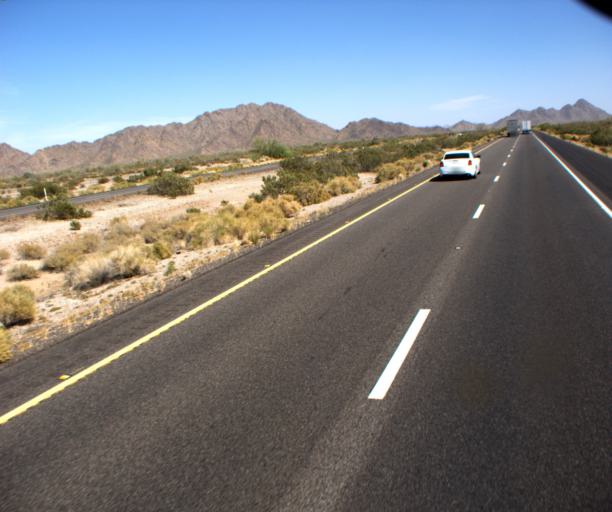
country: US
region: Arizona
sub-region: Maricopa County
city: Gila Bend
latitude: 32.9112
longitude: -112.6080
